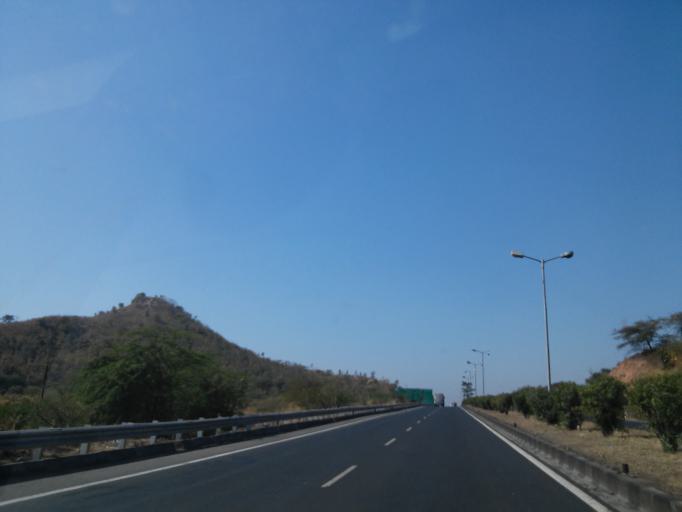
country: IN
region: Gujarat
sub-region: Sabar Kantha
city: Modasa
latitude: 23.6170
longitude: 73.2633
